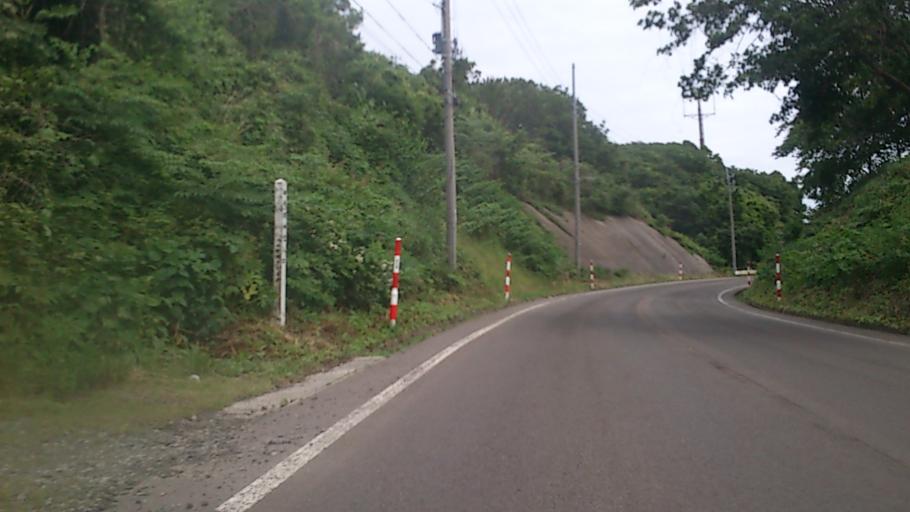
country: JP
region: Akita
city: Noshiromachi
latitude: 40.4278
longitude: 139.9418
